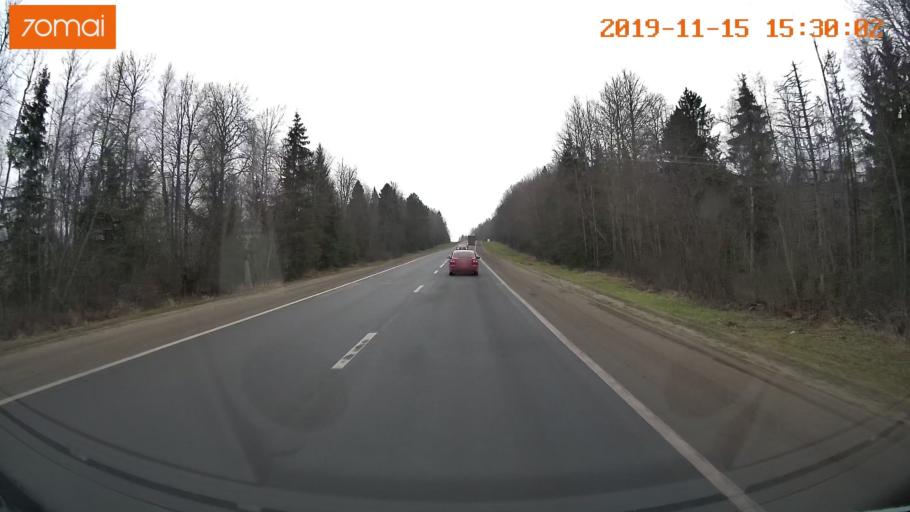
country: RU
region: Jaroslavl
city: Danilov
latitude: 58.1142
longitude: 40.1156
